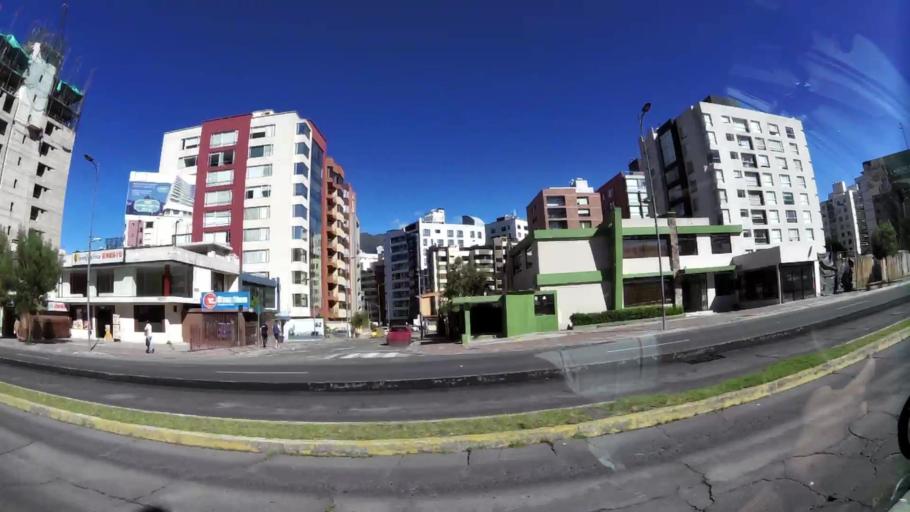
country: EC
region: Pichincha
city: Quito
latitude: -0.1858
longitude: -78.4794
